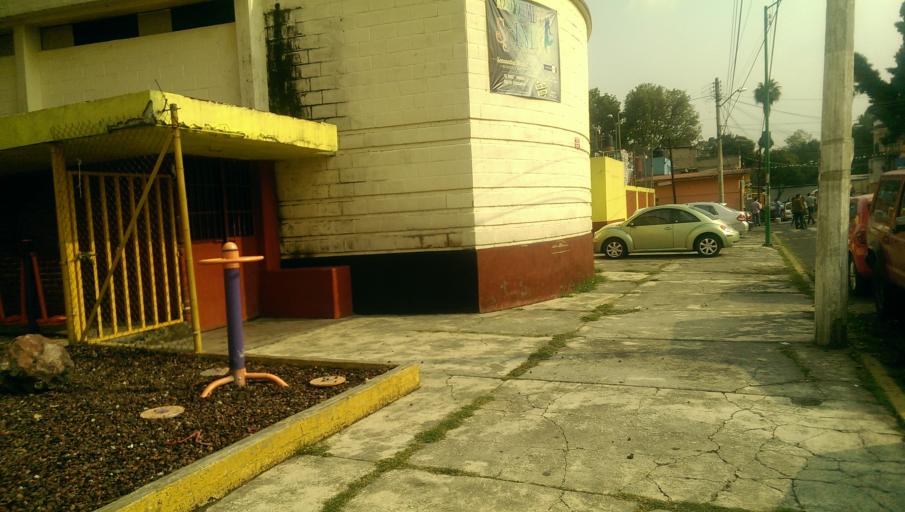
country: MX
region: Mexico City
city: Tlalpan
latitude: 19.2851
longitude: -99.1394
